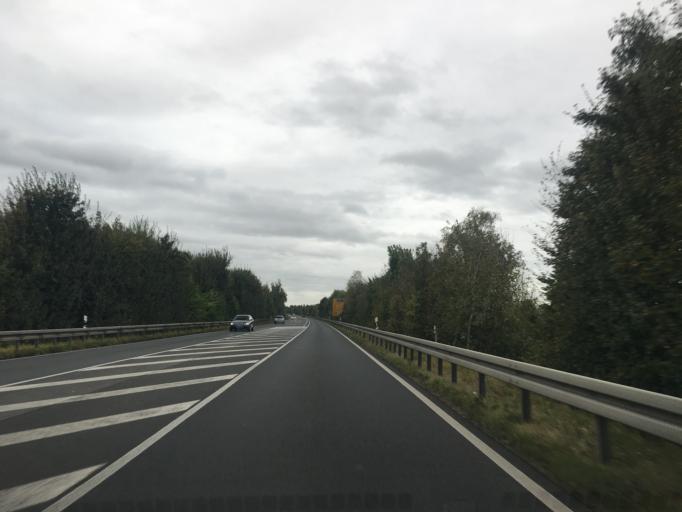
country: DE
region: North Rhine-Westphalia
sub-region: Regierungsbezirk Munster
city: Metelen
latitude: 52.1829
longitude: 7.2400
